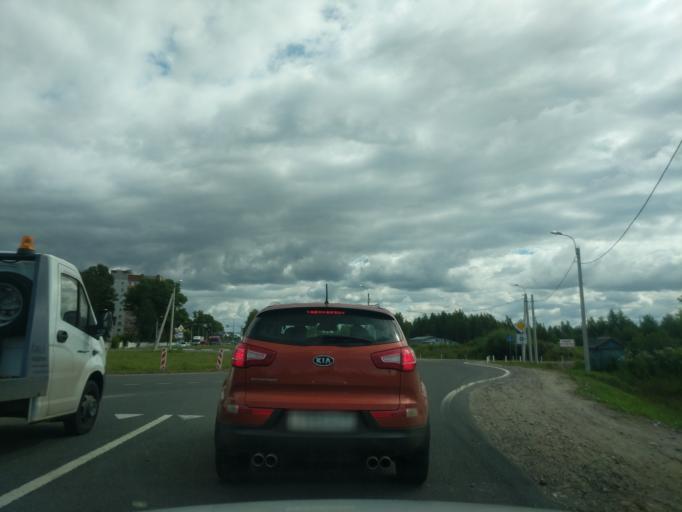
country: RU
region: Jaroslavl
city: Yaroslavl
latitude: 57.5414
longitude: 39.9711
